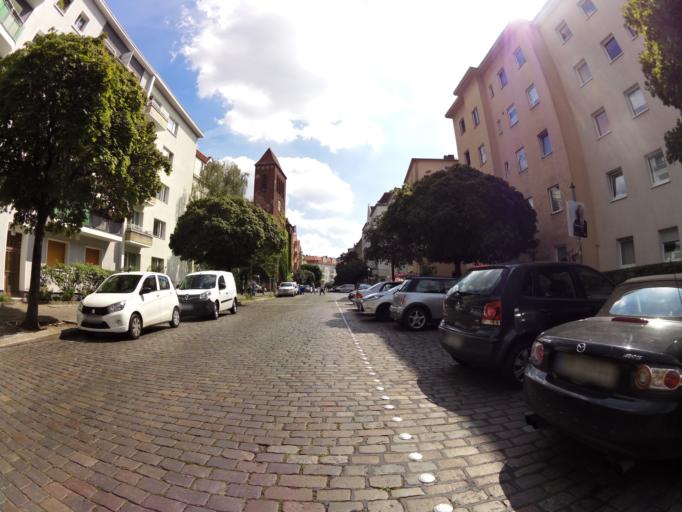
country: DE
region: Berlin
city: Wedding Bezirk
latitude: 52.5421
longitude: 13.3537
